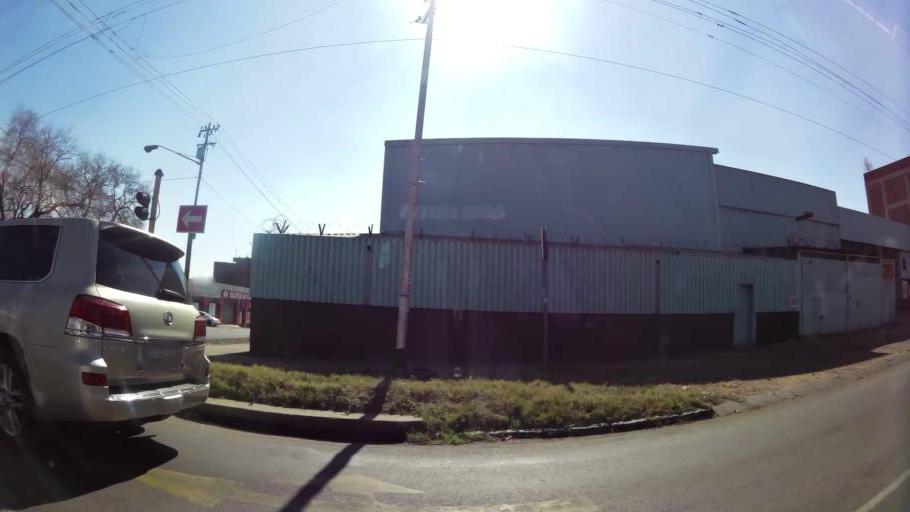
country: ZA
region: Gauteng
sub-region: City of Tshwane Metropolitan Municipality
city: Pretoria
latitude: -25.7545
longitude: 28.1630
